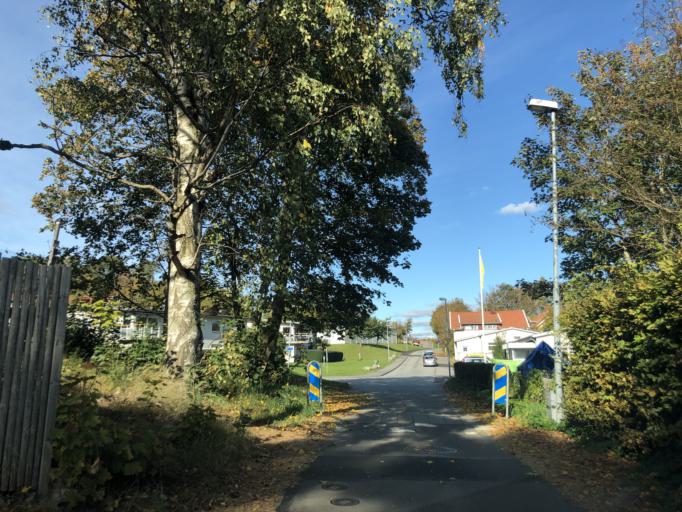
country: SE
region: Vaestra Goetaland
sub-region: Goteborg
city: Billdal
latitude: 57.6286
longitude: 11.9308
